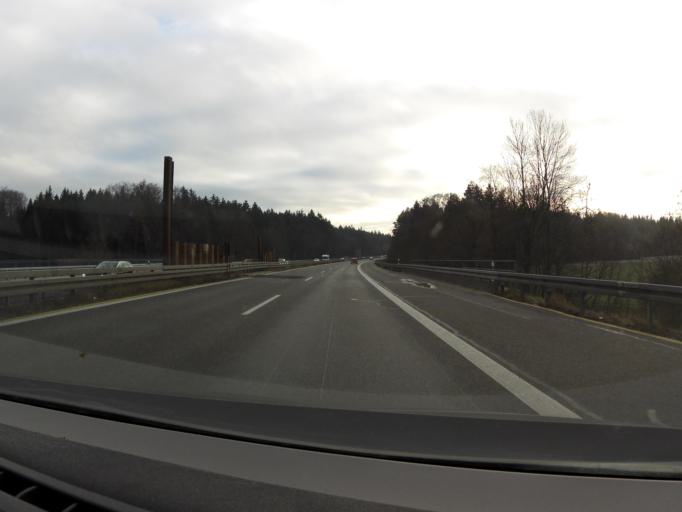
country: DE
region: Bavaria
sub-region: Upper Bavaria
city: Schaftlarn
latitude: 47.9900
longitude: 11.4293
